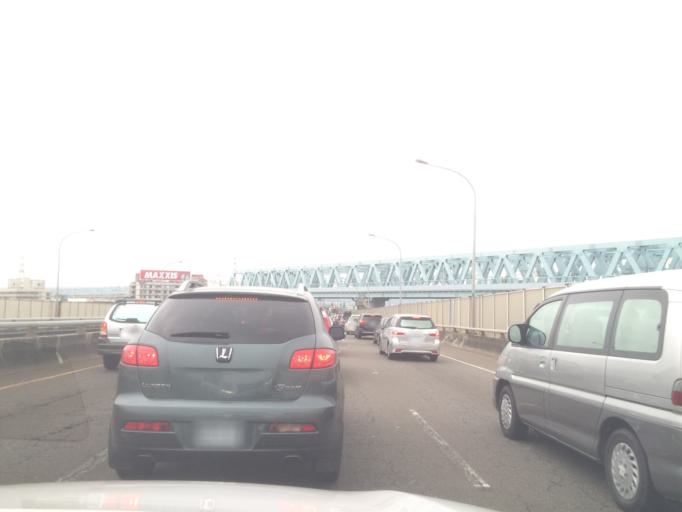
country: TW
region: Taiwan
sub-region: Changhua
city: Chang-hua
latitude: 24.1085
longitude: 120.6177
